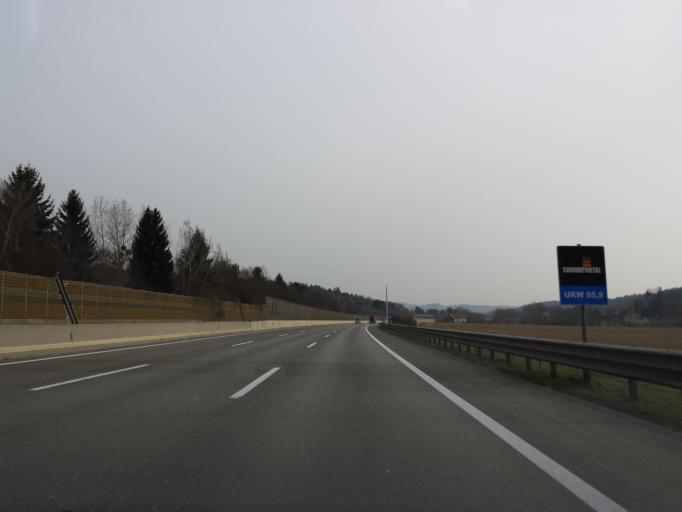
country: AT
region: Styria
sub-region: Politischer Bezirk Weiz
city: Ungerdorf
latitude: 47.0835
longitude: 15.6514
